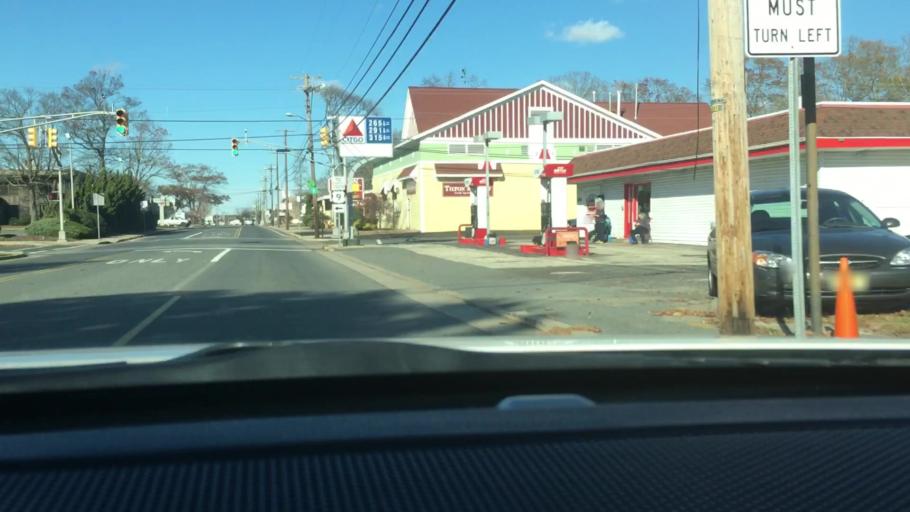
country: US
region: New Jersey
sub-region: Atlantic County
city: Northfield
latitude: 39.3698
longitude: -74.5527
